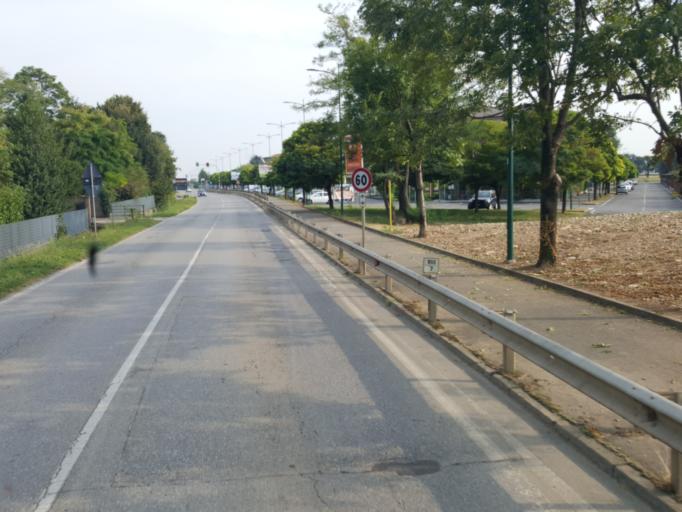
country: IT
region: Lombardy
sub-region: Provincia di Bergamo
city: Cavernago
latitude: 45.6244
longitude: 9.7708
